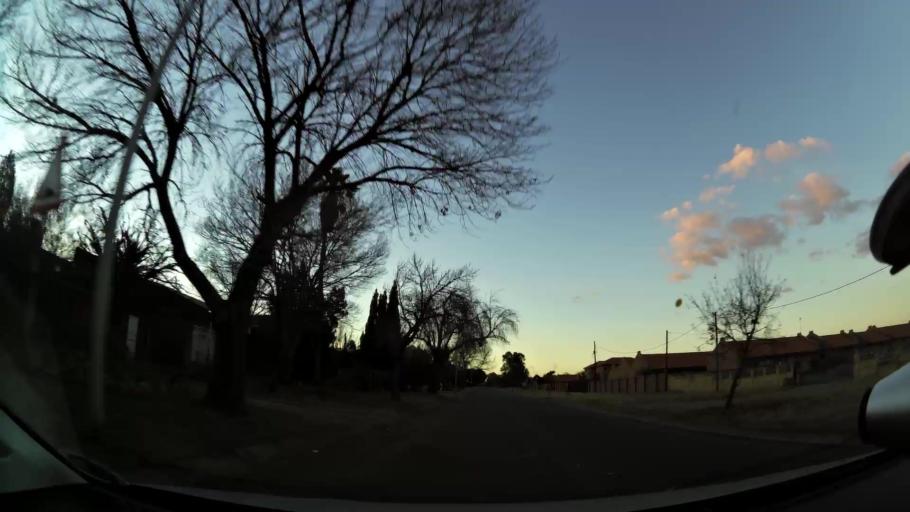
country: ZA
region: North-West
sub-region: Dr Kenneth Kaunda District Municipality
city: Potchefstroom
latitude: -26.7191
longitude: 27.1232
